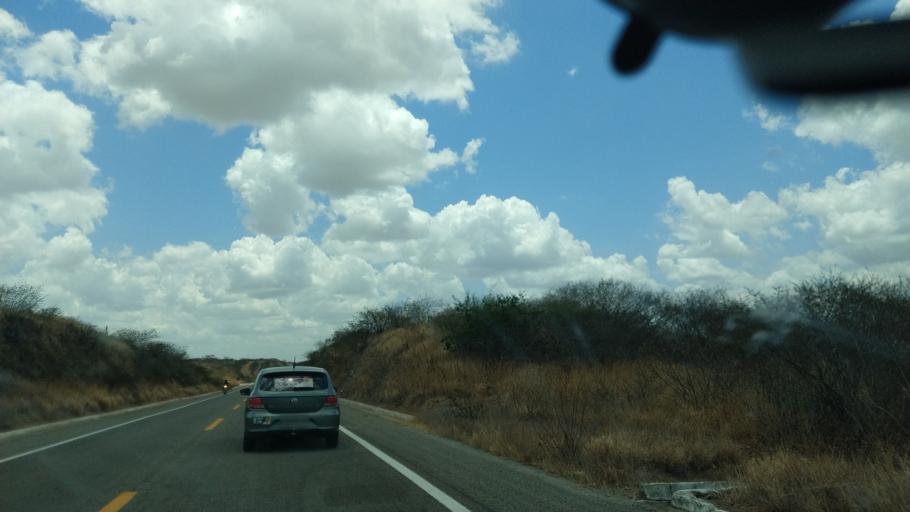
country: BR
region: Rio Grande do Norte
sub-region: Cerro Cora
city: Cerro Cora
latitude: -6.2099
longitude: -36.2963
